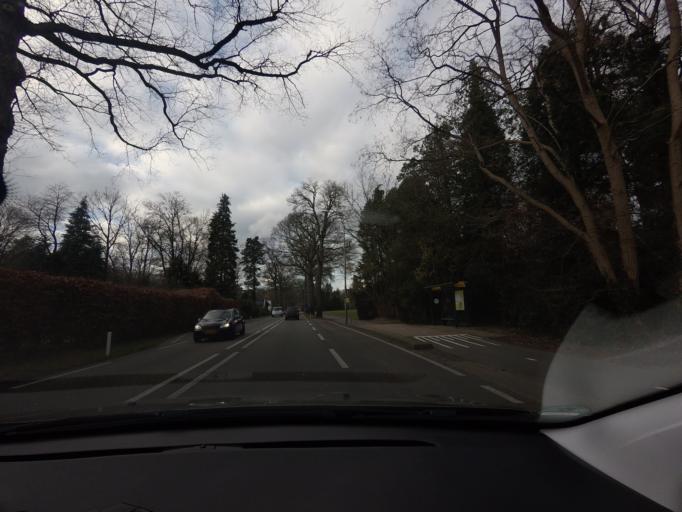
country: NL
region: Gelderland
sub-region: Gemeente Lochem
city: Eefde
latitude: 52.1822
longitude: 6.2147
